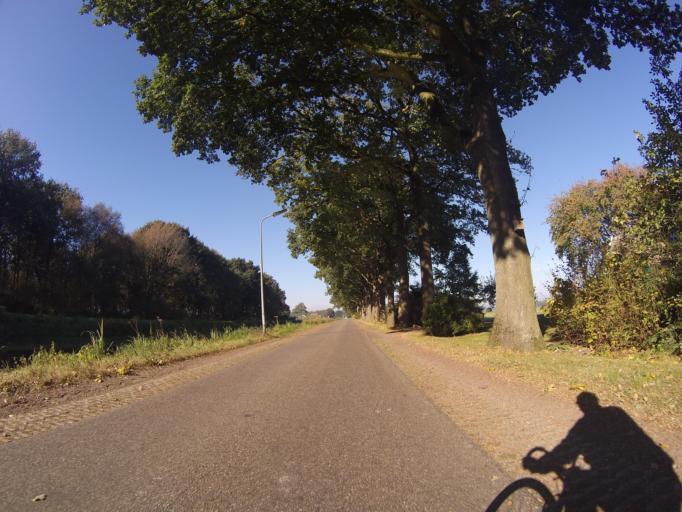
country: NL
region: Drenthe
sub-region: Gemeente Coevorden
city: Dalen
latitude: 52.7393
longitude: 6.7722
